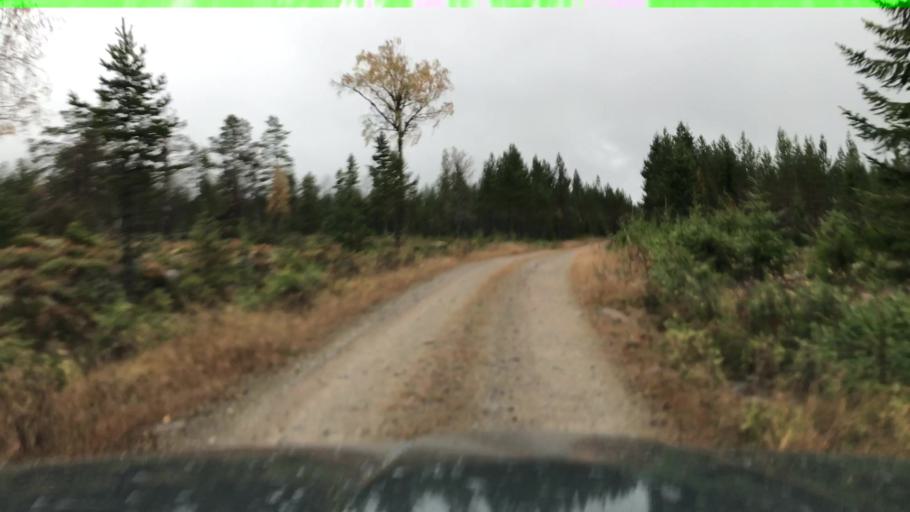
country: NO
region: Hedmark
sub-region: Trysil
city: Innbygda
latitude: 60.9287
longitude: 12.6508
